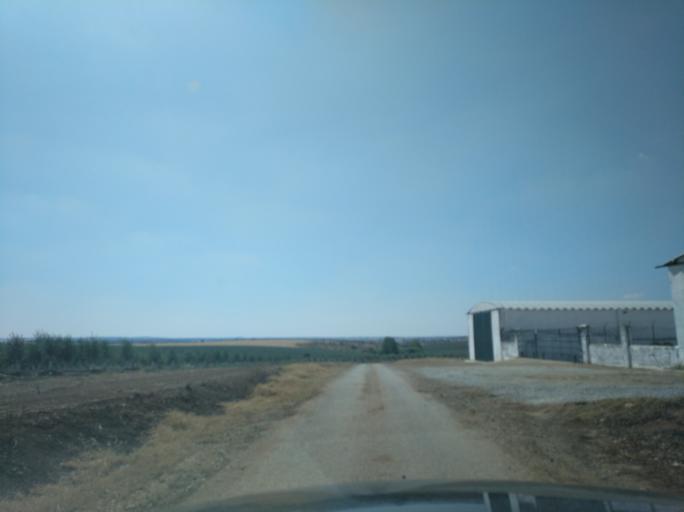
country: PT
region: Portalegre
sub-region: Campo Maior
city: Campo Maior
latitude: 39.0232
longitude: -7.1258
